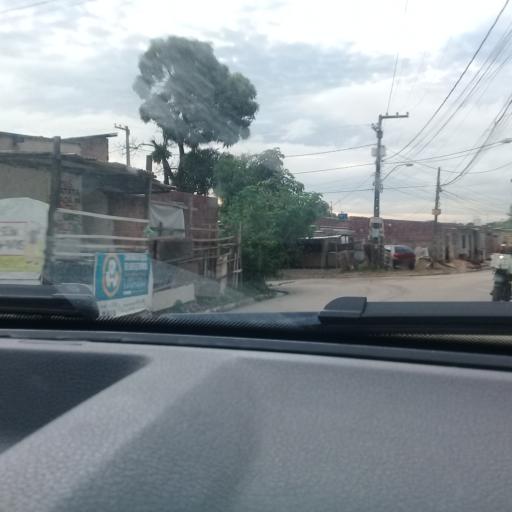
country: BR
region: Pernambuco
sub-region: Jaboatao Dos Guararapes
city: Jaboatao dos Guararapes
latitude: -8.1088
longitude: -34.9552
